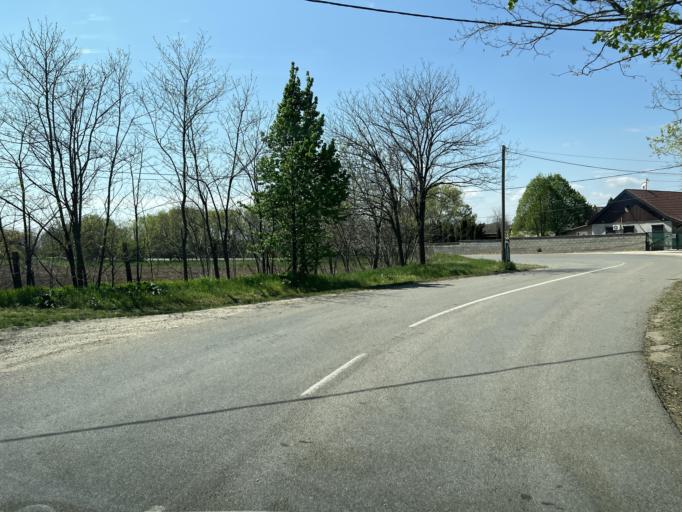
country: HU
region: Pest
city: Inarcs
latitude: 47.2452
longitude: 19.3195
